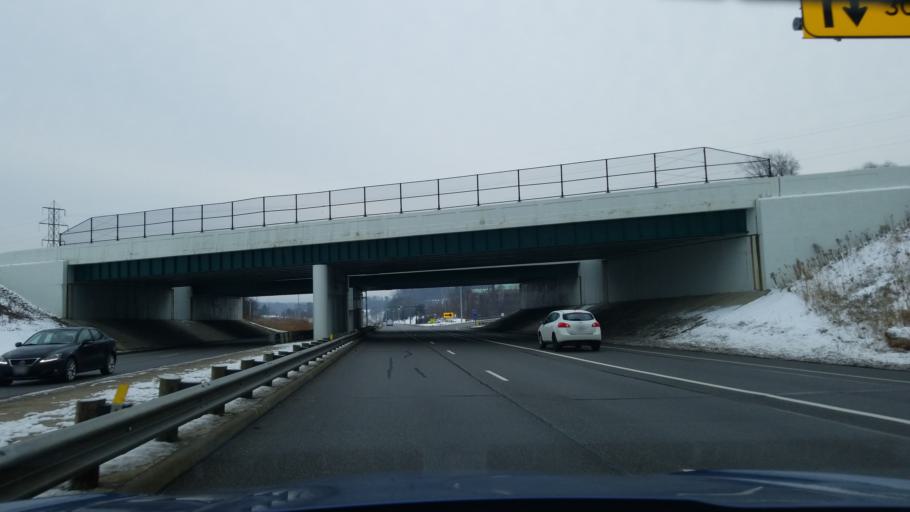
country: US
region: Ohio
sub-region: Cuyahoga County
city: Brecksville
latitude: 41.3162
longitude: -81.6497
